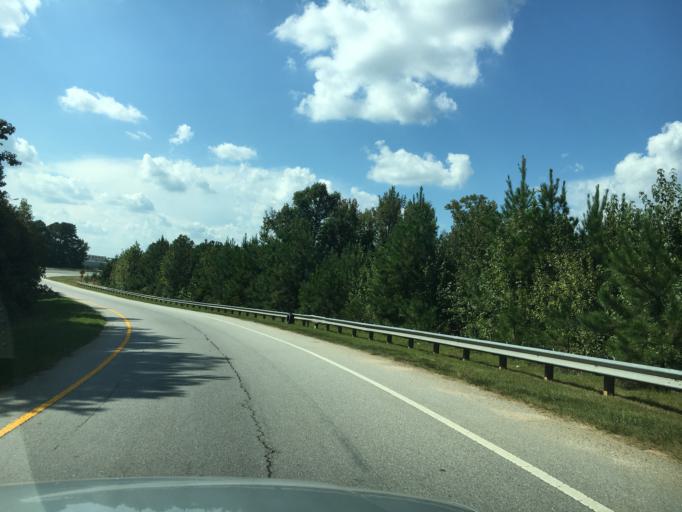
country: US
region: South Carolina
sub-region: Greenville County
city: Fountain Inn
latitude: 34.6435
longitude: -82.1474
